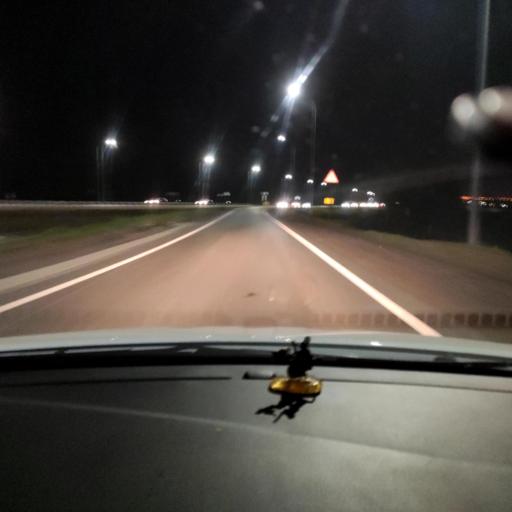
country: RU
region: Tatarstan
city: Vysokaya Gora
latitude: 55.8128
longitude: 49.4316
